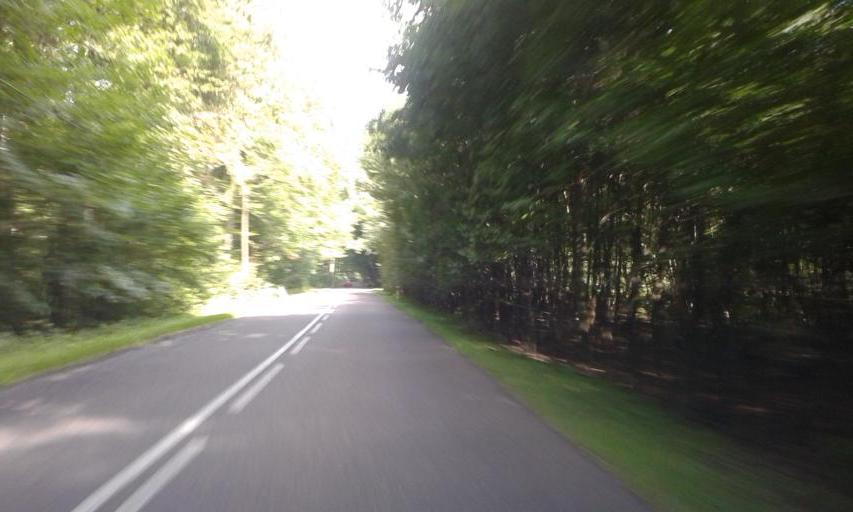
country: PL
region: West Pomeranian Voivodeship
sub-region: Powiat slawienski
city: Slawno
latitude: 54.2616
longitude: 16.6808
